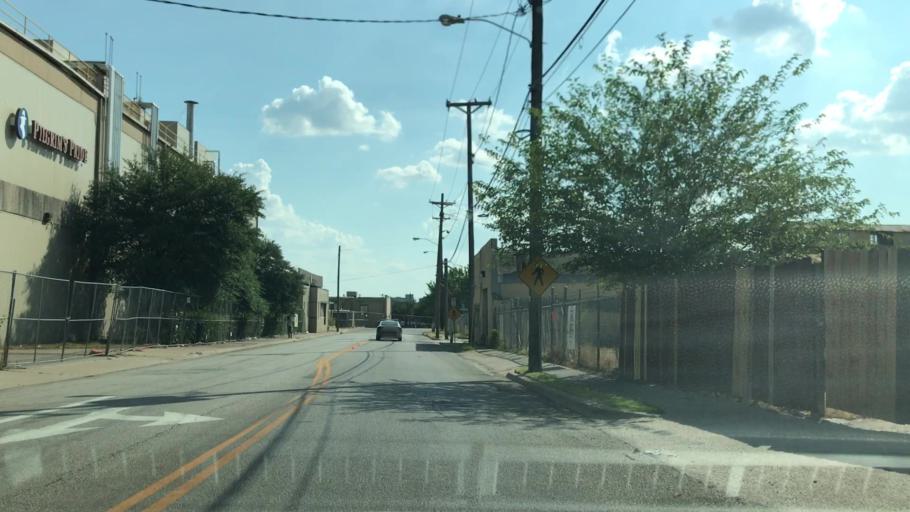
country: US
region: Texas
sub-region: Dallas County
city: Dallas
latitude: 32.7745
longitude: -96.7810
